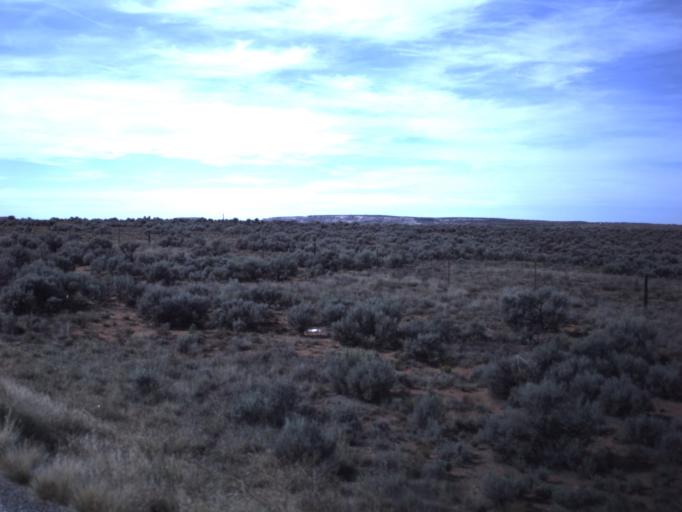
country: US
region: Utah
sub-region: San Juan County
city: Blanding
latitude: 37.4135
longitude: -109.3350
